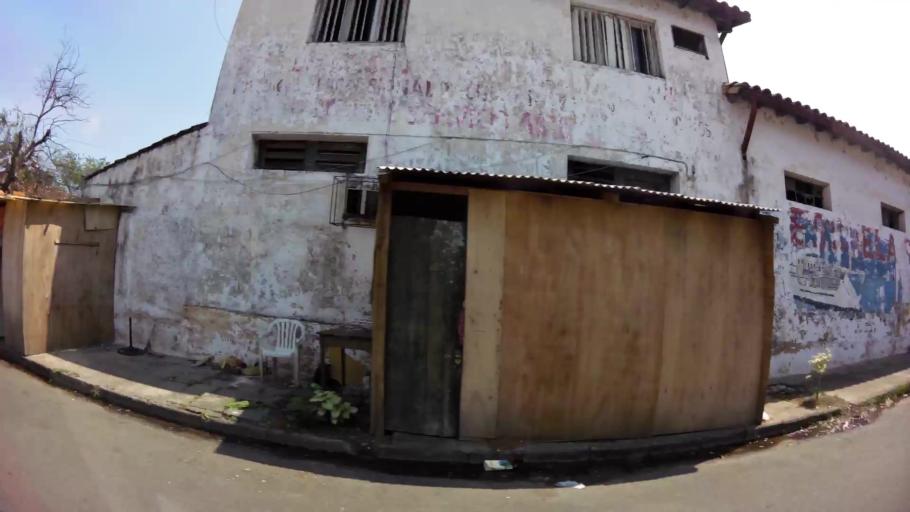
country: PY
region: Presidente Hayes
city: Nanawa
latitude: -25.2770
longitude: -57.6533
